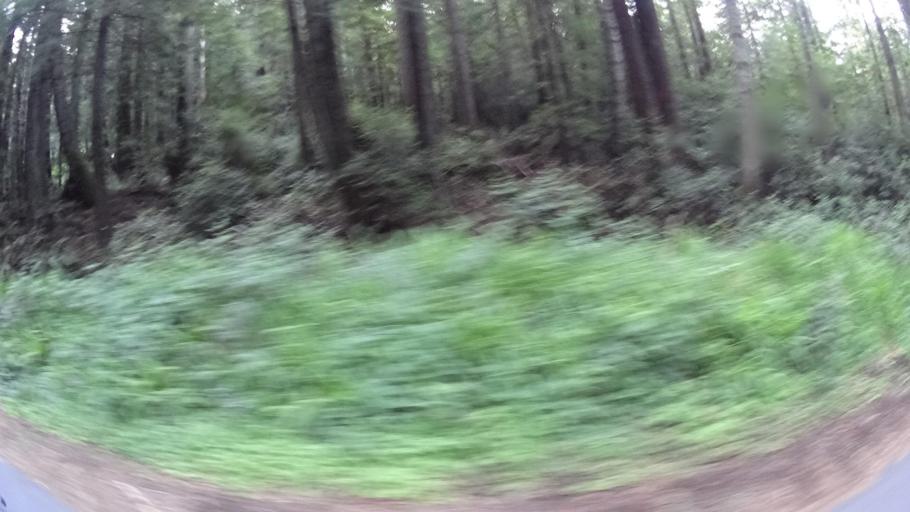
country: US
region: California
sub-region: Humboldt County
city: Bayside
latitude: 40.7627
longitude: -124.0004
